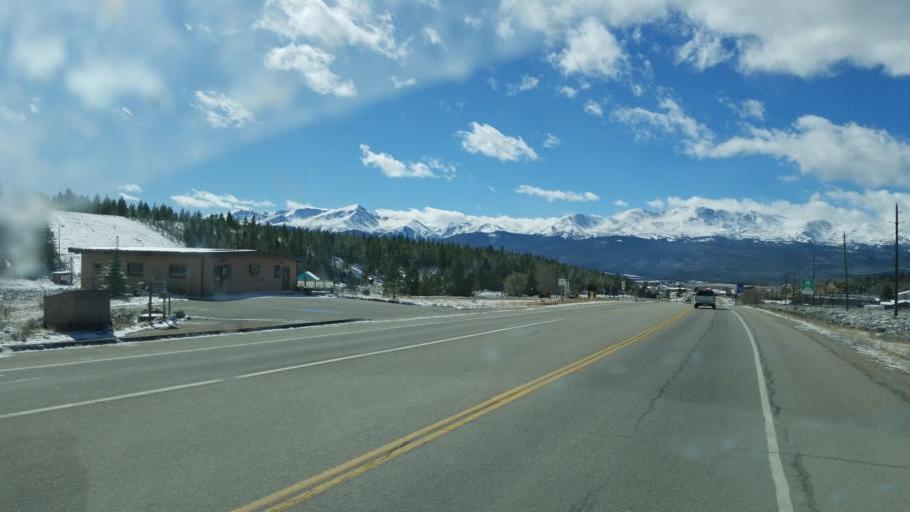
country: US
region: Colorado
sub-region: Lake County
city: Leadville
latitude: 39.2402
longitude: -106.3026
